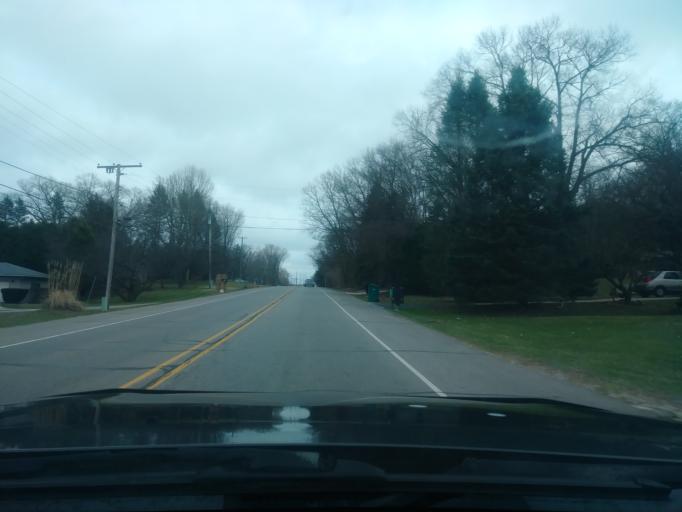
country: US
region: Indiana
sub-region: LaPorte County
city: Trail Creek
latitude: 41.6477
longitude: -86.8069
